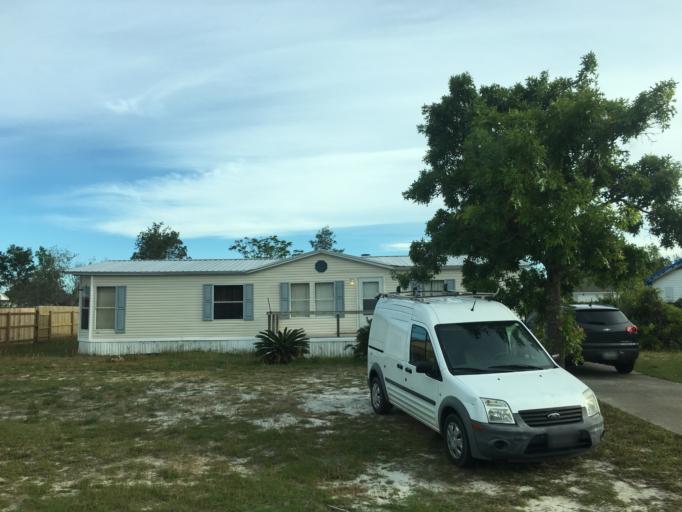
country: US
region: Florida
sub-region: Bay County
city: Upper Grand Lagoon
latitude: 30.1700
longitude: -85.7694
